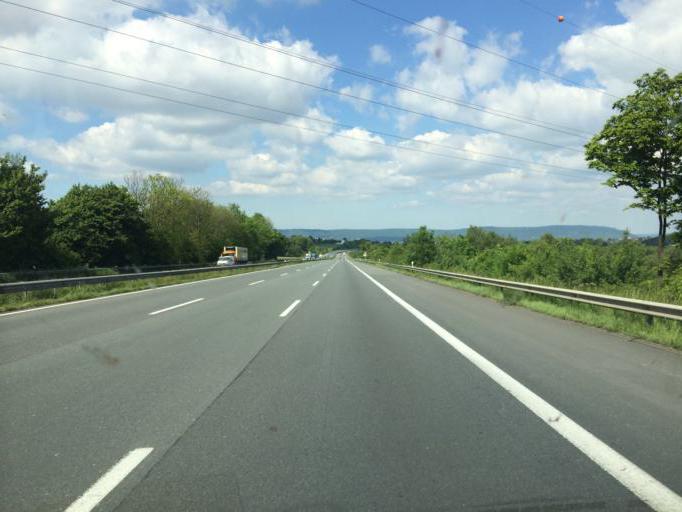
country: DE
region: North Rhine-Westphalia
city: Bad Oeynhausen
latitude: 52.1628
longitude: 8.8131
